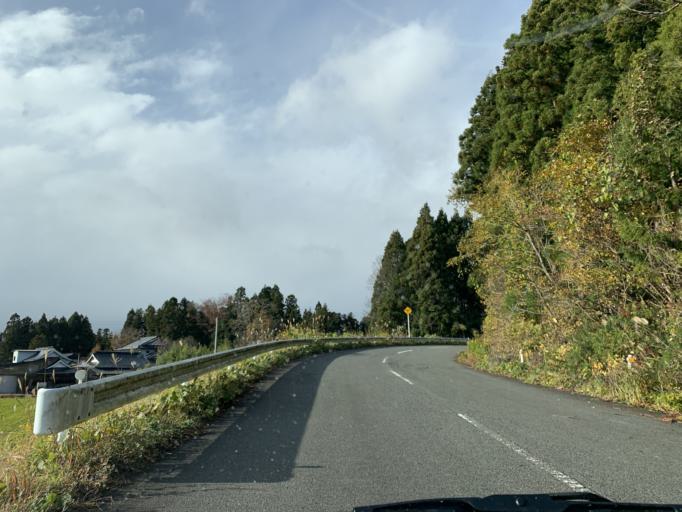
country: JP
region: Iwate
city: Mizusawa
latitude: 39.0298
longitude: 141.0724
